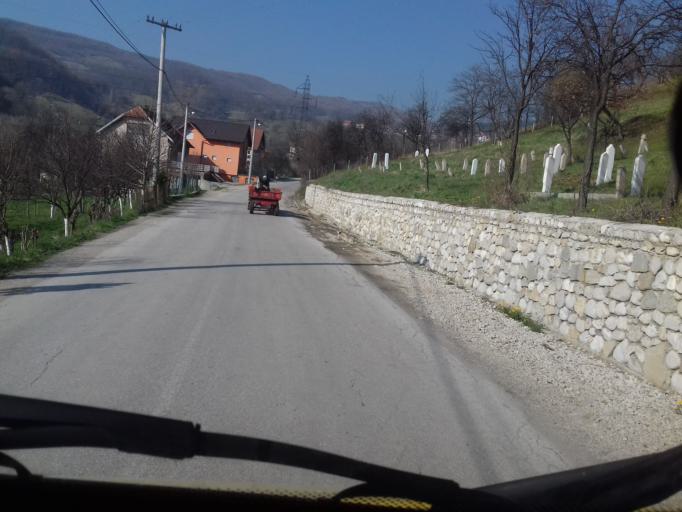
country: BA
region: Federation of Bosnia and Herzegovina
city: Lokvine
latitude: 44.2295
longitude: 17.8441
